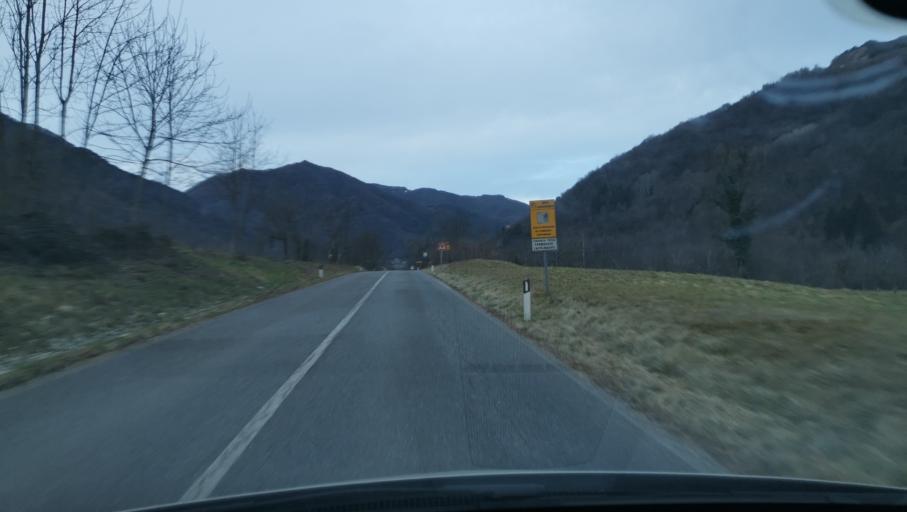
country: IT
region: Piedmont
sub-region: Provincia di Cuneo
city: Monterosso Grana
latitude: 44.4109
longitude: 7.3375
